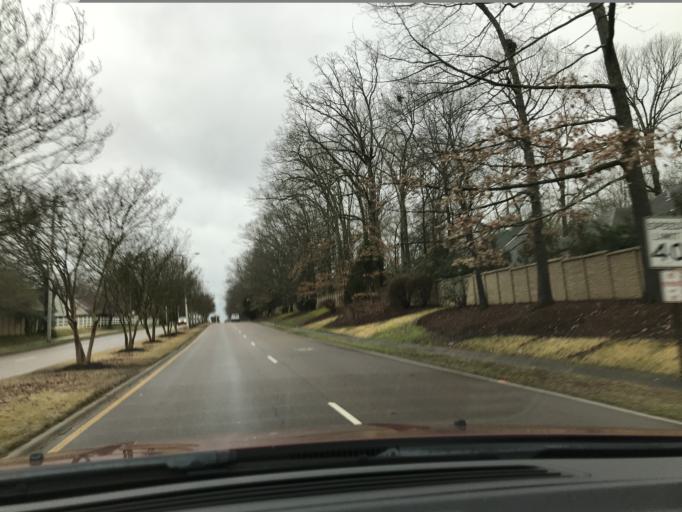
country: US
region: Tennessee
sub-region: Shelby County
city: Collierville
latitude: 35.0675
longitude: -89.6858
